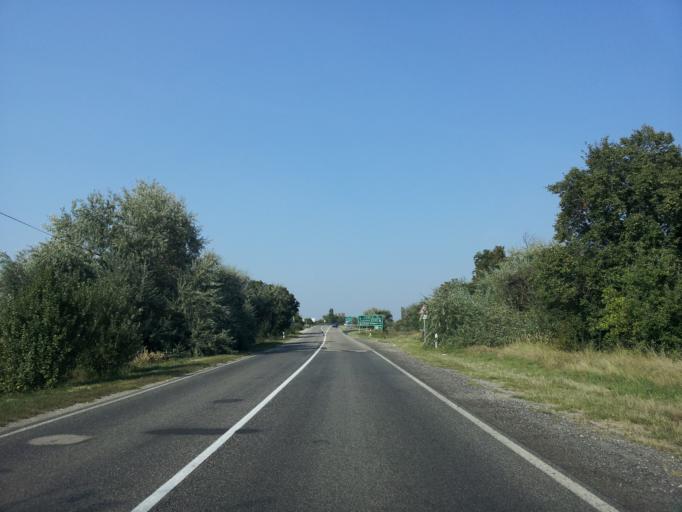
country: HU
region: Fejer
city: Polgardi
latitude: 47.0380
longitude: 18.2939
